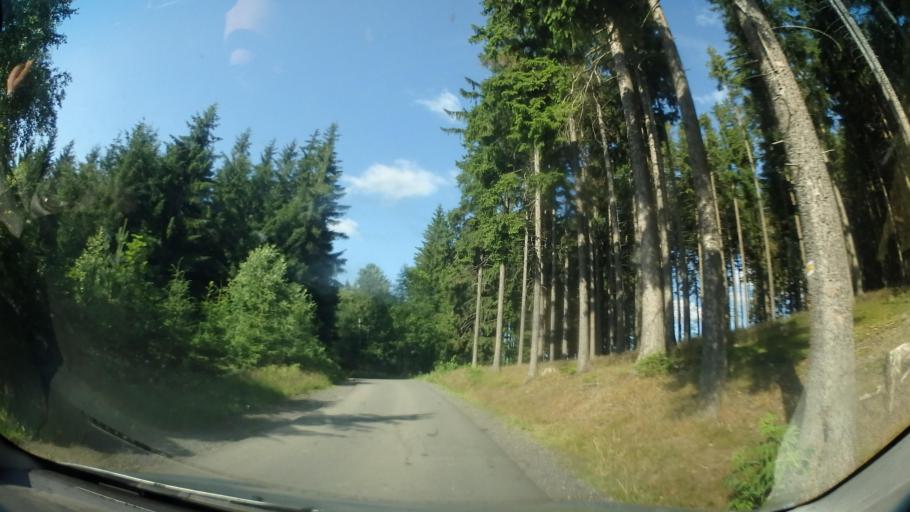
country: CZ
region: Vysocina
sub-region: Okres Zd'ar nad Sazavou
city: Svratka
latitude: 49.7266
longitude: 16.0442
